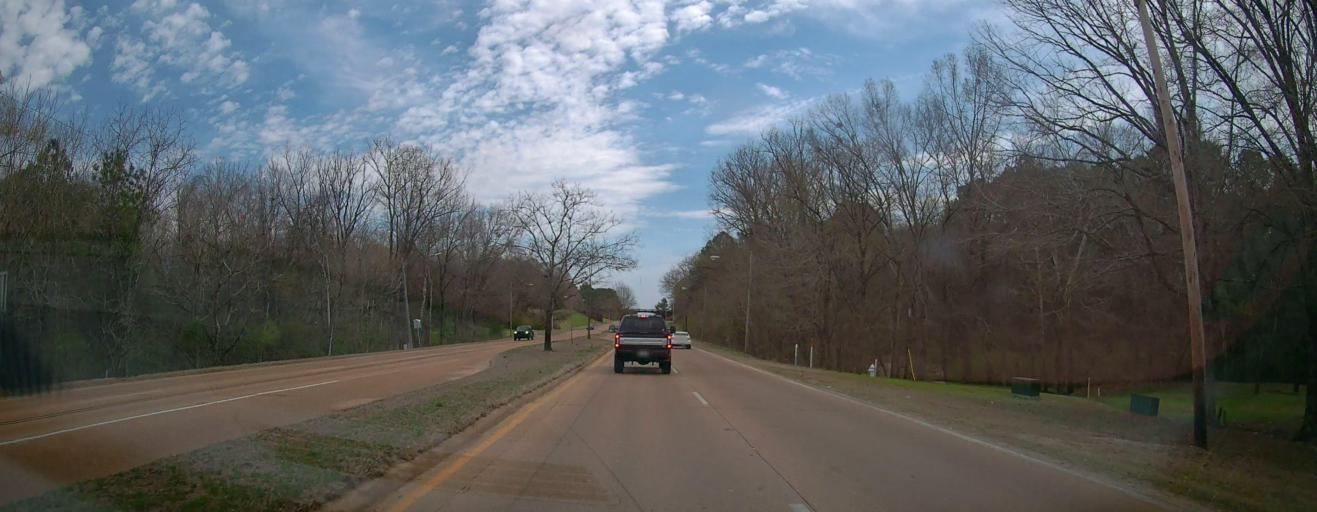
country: US
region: Mississippi
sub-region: Lee County
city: Tupelo
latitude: 34.2837
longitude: -88.7355
